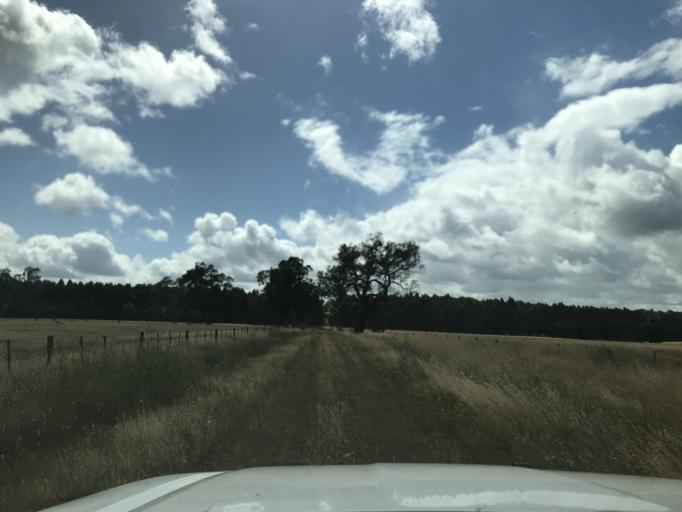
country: AU
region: South Australia
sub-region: Wattle Range
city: Penola
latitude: -37.1914
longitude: 141.3930
